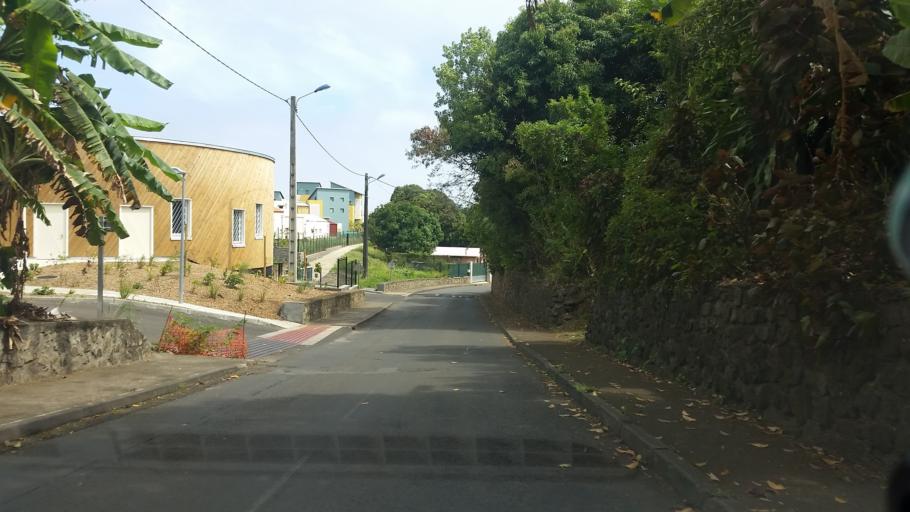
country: RE
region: Reunion
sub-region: Reunion
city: Sainte-Marie
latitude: -20.9213
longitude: 55.5313
